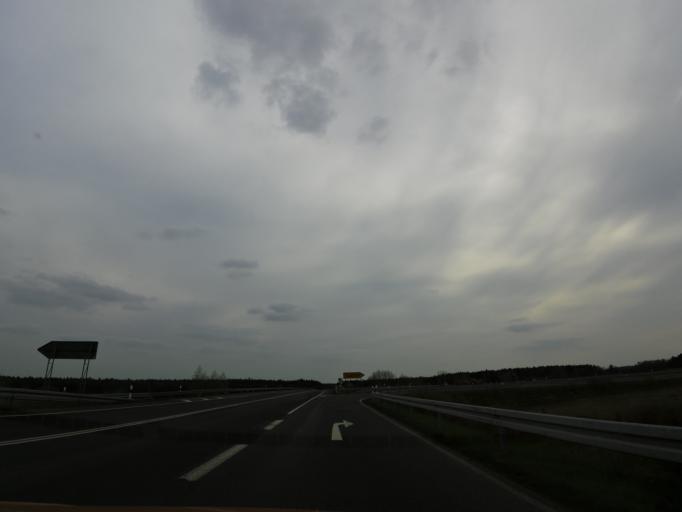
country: DE
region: Brandenburg
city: Beeskow
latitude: 52.1678
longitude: 14.2168
